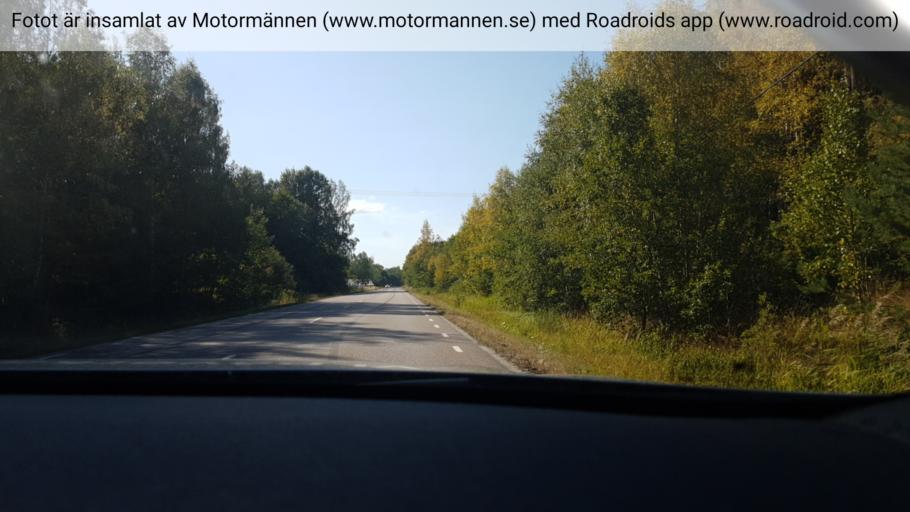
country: SE
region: Vaestra Goetaland
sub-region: Gotene Kommun
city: Goetene
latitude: 58.6259
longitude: 13.4625
